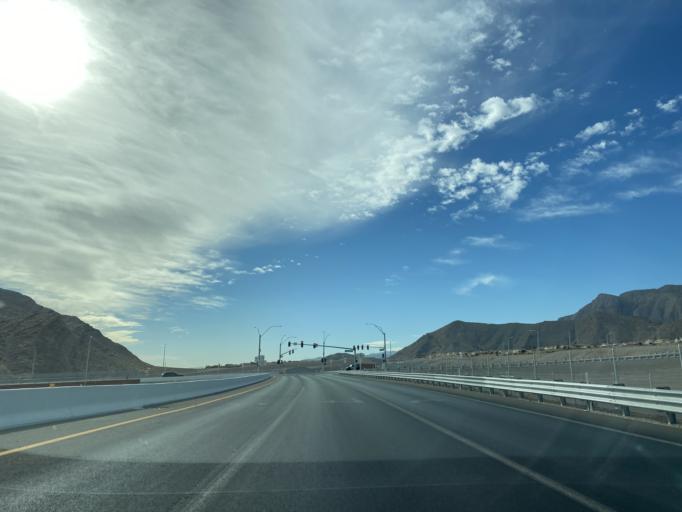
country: US
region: Nevada
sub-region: Clark County
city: Summerlin South
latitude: 36.2493
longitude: -115.3185
